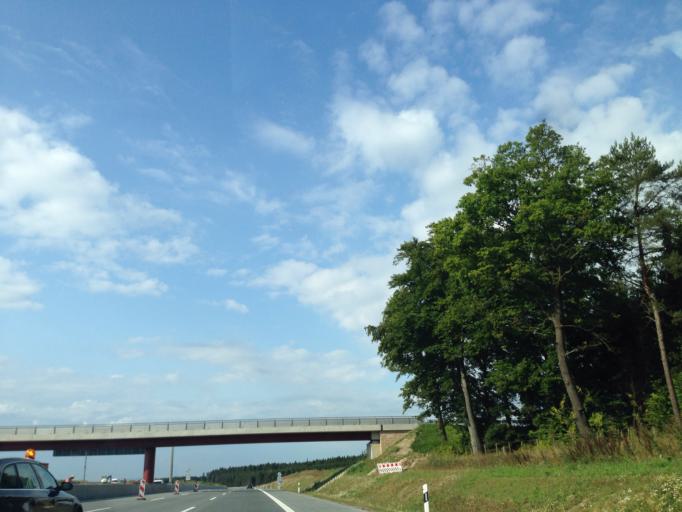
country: DE
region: Thuringia
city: Dittersdorf
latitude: 50.6531
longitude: 11.8088
